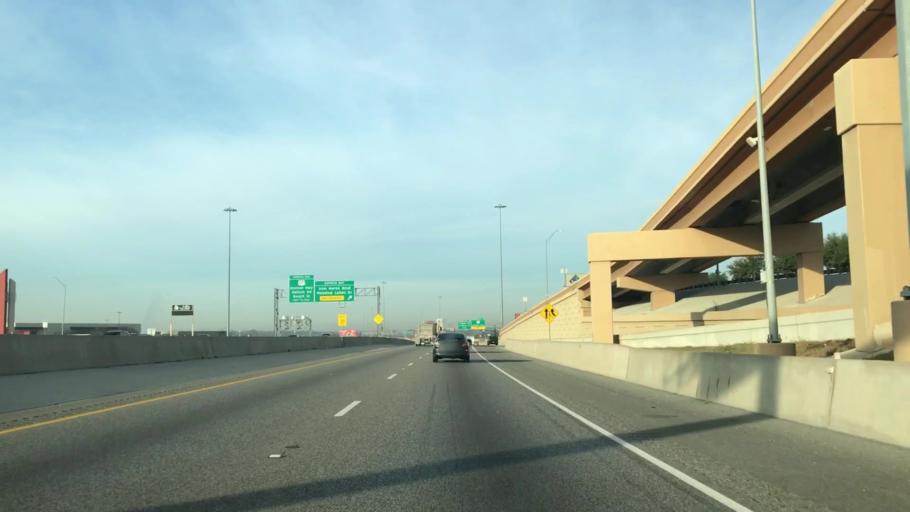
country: US
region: Texas
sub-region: Tarrant County
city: North Richland Hills
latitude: 32.8404
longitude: -97.2455
